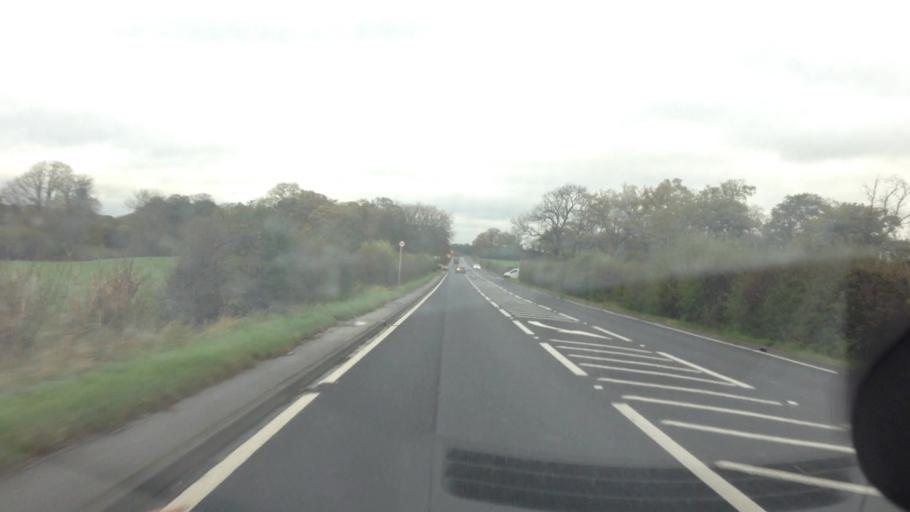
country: GB
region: England
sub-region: City and Borough of Leeds
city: Shadwell
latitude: 53.8481
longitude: -1.4652
